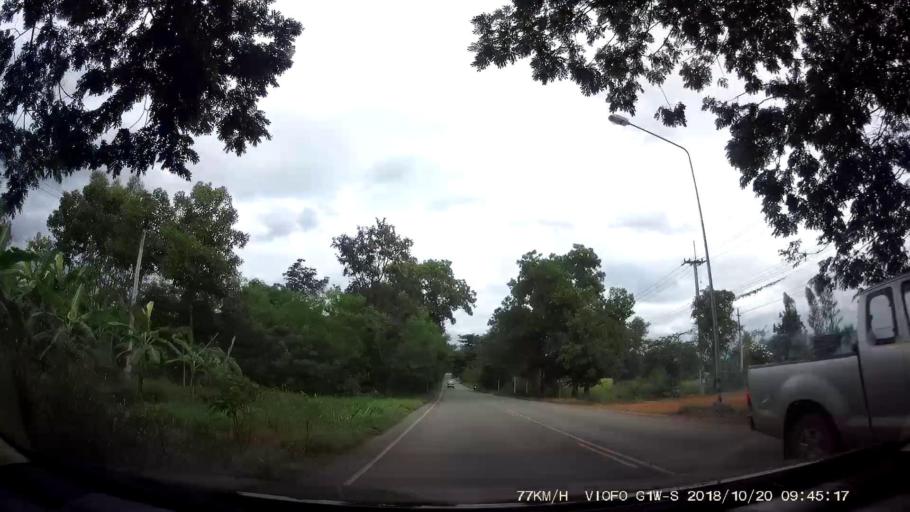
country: TH
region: Chaiyaphum
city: Khon San
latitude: 16.4902
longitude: 101.9381
